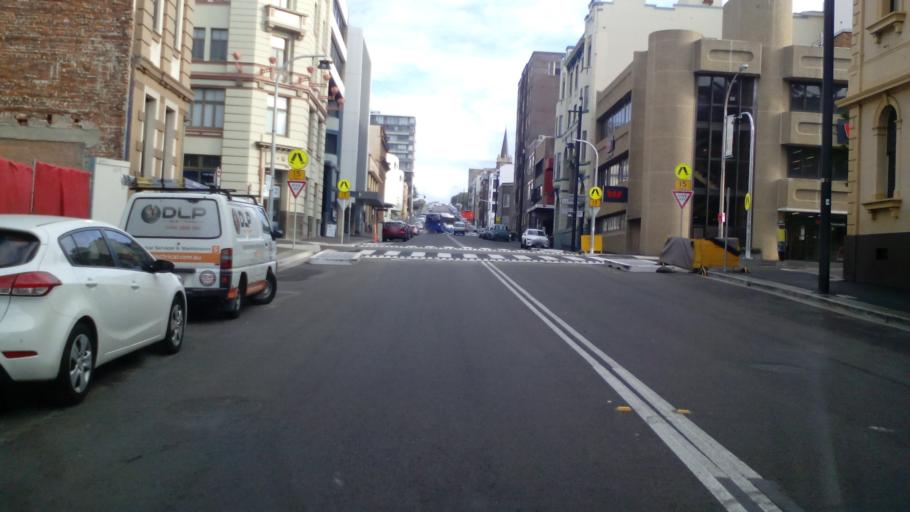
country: AU
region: New South Wales
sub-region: Newcastle
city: Newcastle
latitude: -32.9275
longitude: 151.7844
